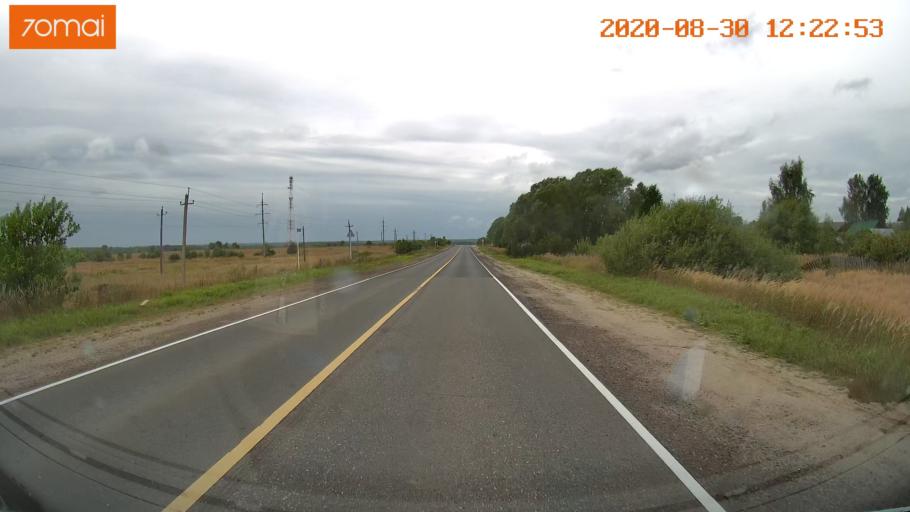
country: RU
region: Ivanovo
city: Yur'yevets
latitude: 57.3312
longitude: 42.8391
